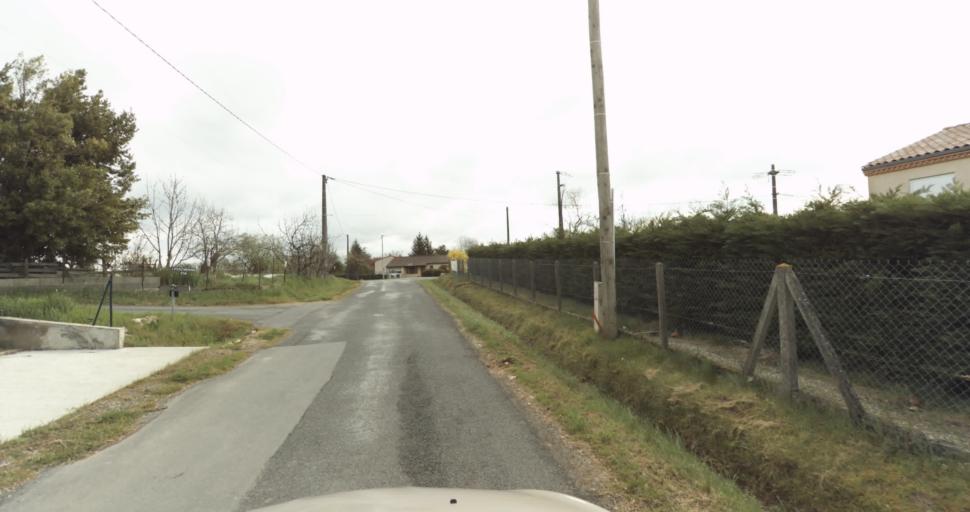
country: FR
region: Midi-Pyrenees
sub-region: Departement du Tarn
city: Frejairolles
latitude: 43.8649
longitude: 2.2209
